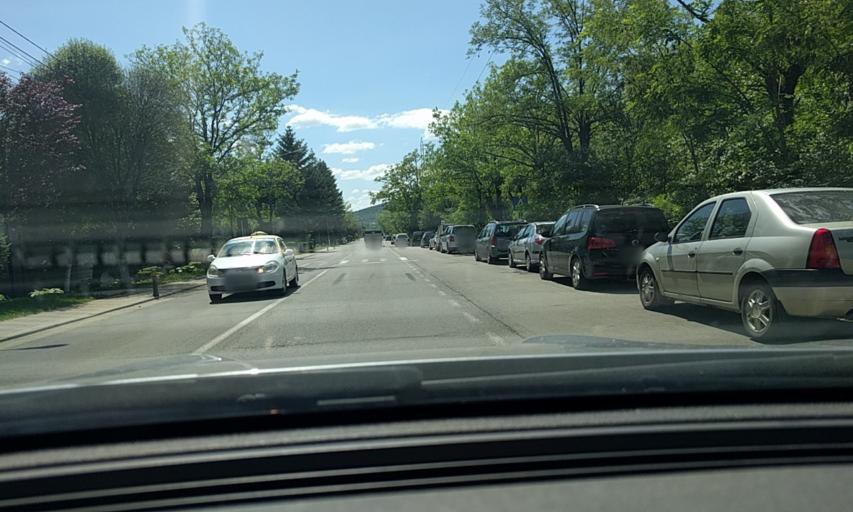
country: RO
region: Bistrita-Nasaud
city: Bistrita
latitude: 47.1320
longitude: 24.4718
